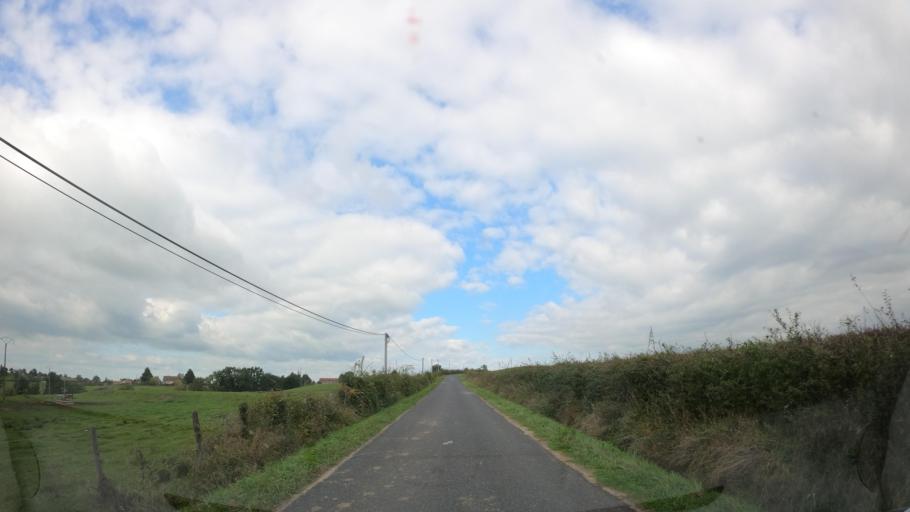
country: FR
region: Auvergne
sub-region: Departement de l'Allier
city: Lapalisse
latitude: 46.3394
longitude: 3.6377
